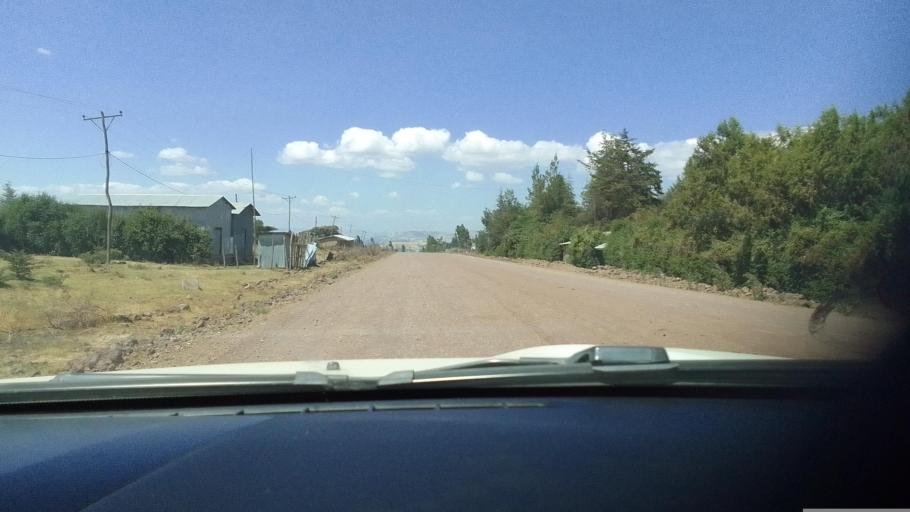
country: ET
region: Oromiya
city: Hagere Hiywet
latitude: 8.9196
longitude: 37.8670
